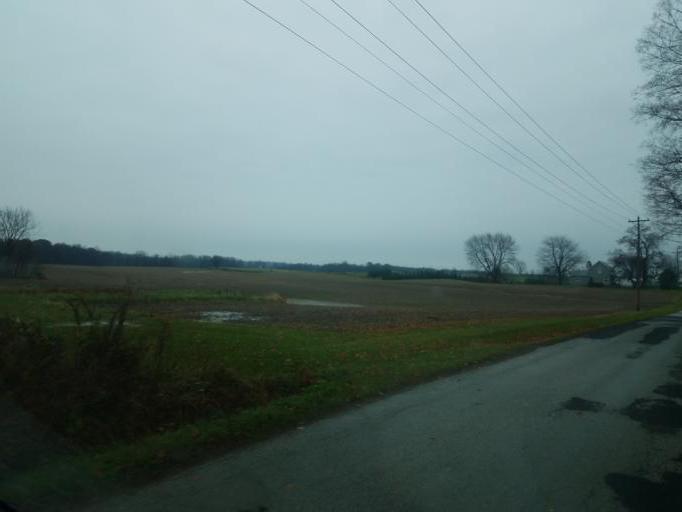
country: US
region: Ohio
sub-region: Knox County
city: Centerburg
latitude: 40.3494
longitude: -82.7403
